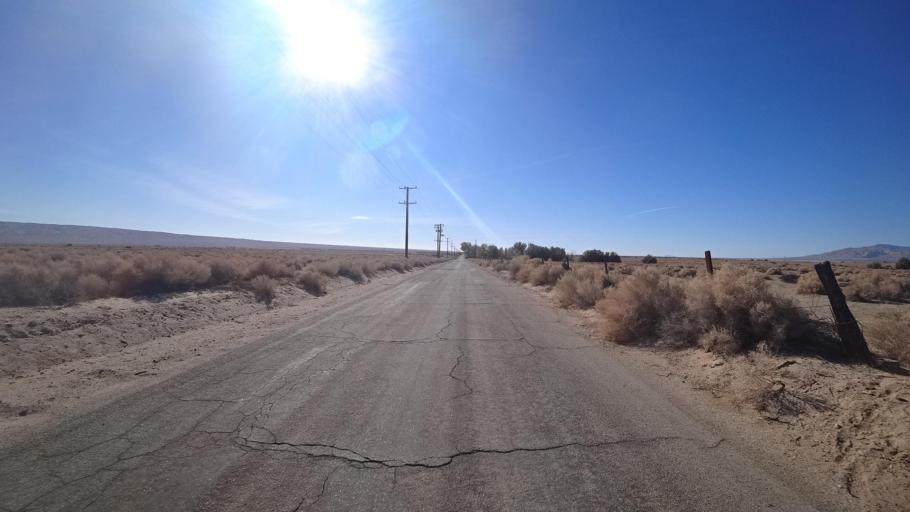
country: US
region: California
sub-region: Kern County
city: California City
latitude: 35.3052
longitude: -117.9503
